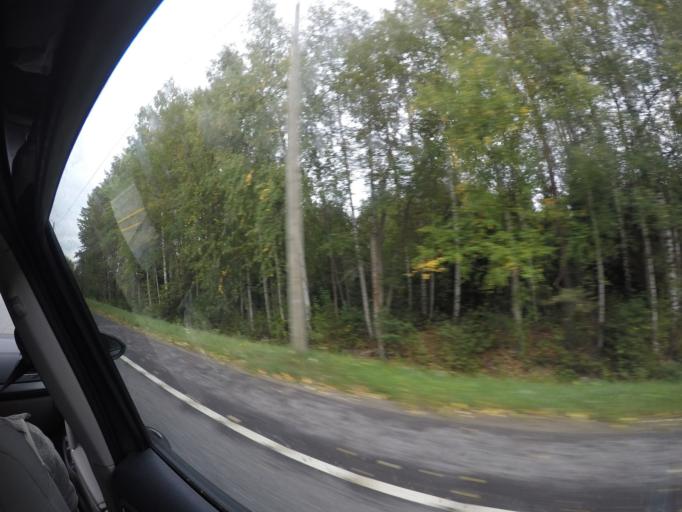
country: FI
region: Haeme
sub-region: Haemeenlinna
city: Parola
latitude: 61.1813
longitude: 24.4134
